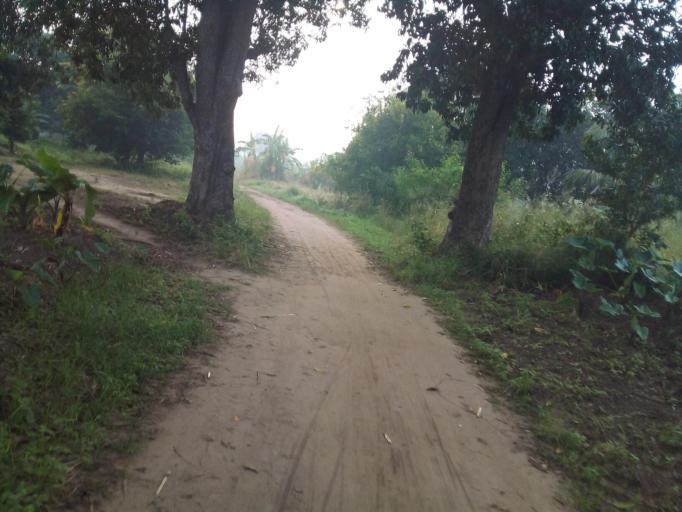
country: MZ
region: Zambezia
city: Quelimane
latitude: -17.5876
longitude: 36.6851
